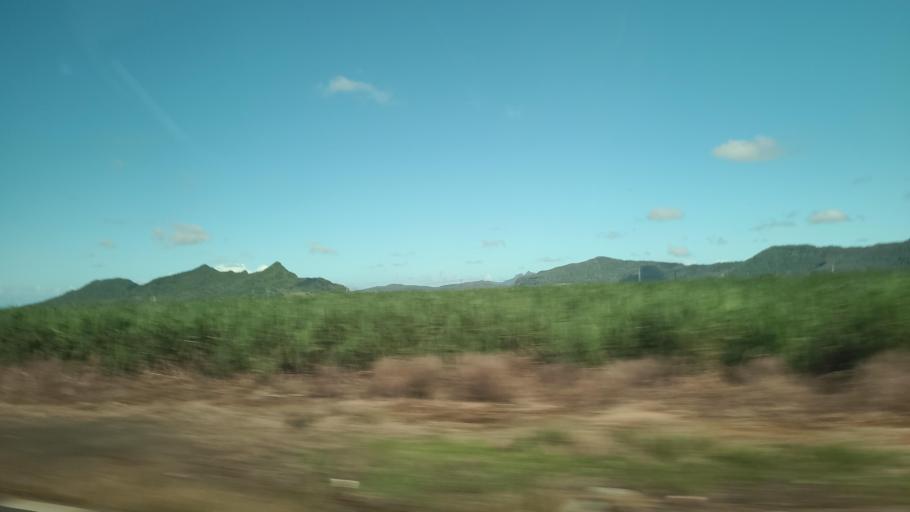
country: MU
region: Flacq
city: Camp de Masque
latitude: -20.2306
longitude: 57.6593
